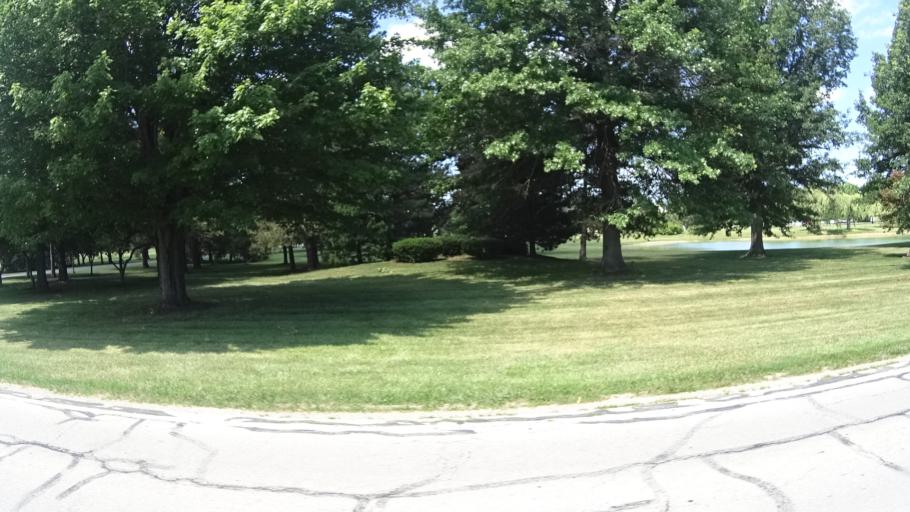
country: US
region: Ohio
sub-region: Erie County
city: Huron
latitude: 41.3974
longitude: -82.5910
